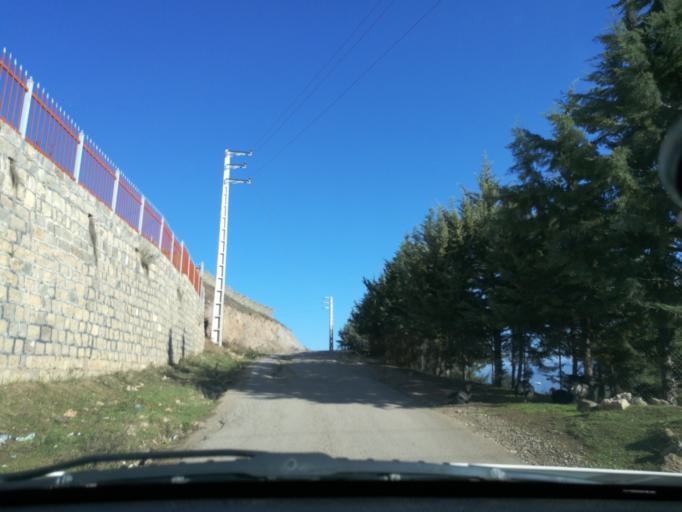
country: IR
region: Mazandaran
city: `Abbasabad
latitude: 36.5590
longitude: 51.1887
